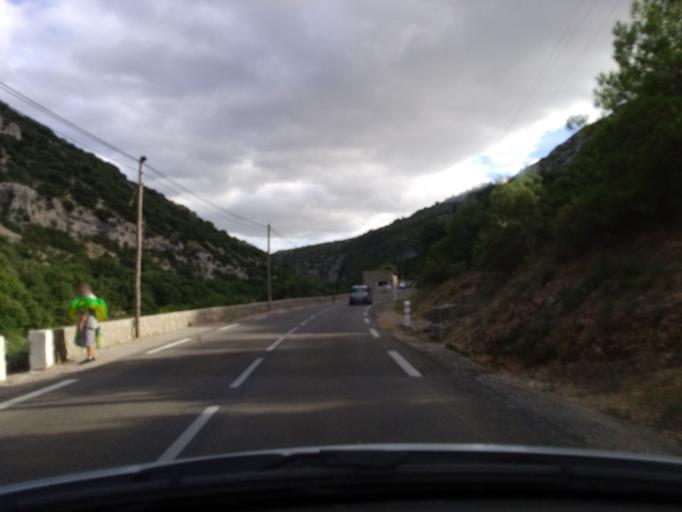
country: FR
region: Languedoc-Roussillon
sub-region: Departement de l'Herault
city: Saint-Jean-de-Fos
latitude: 43.7189
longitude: 3.5534
